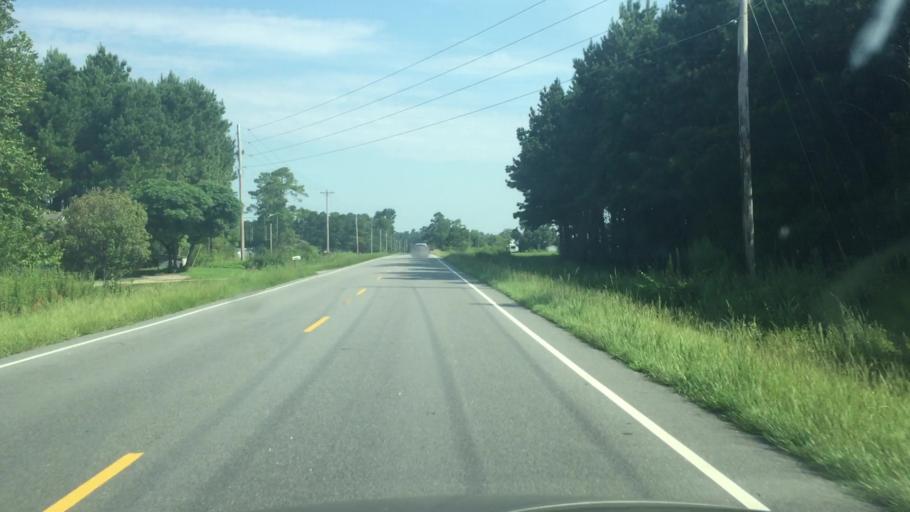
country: US
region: North Carolina
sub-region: Columbus County
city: Tabor City
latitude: 34.2246
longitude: -78.8242
